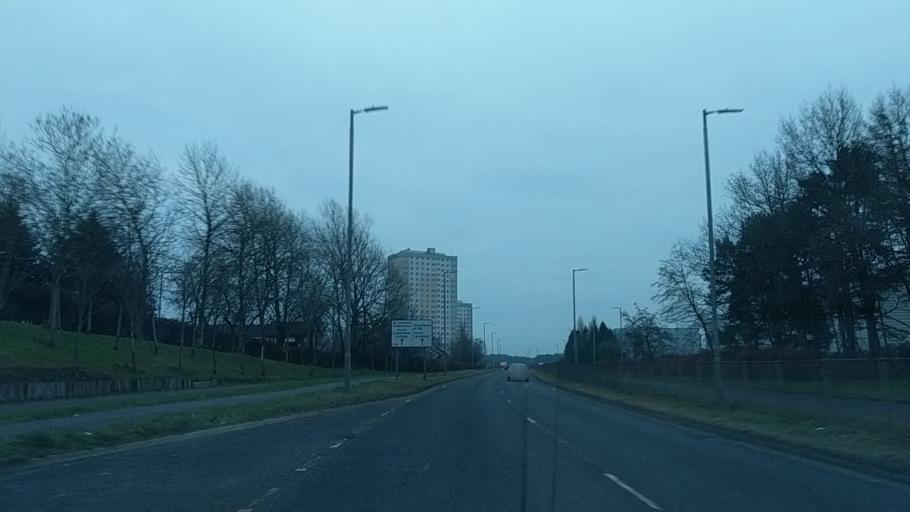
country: GB
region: Scotland
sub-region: South Lanarkshire
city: East Kilbride
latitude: 55.7571
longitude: -4.1632
